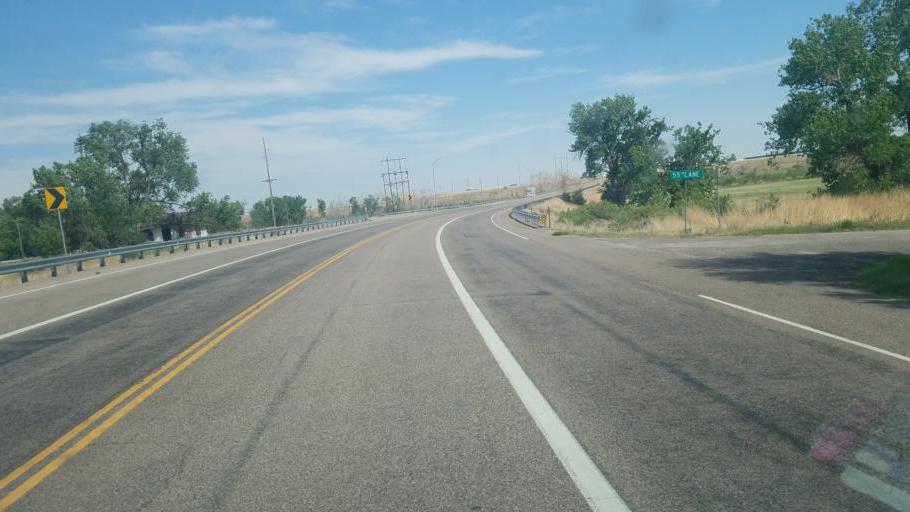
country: US
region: Colorado
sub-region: Otero County
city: Fowler
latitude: 38.2279
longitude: -104.2642
